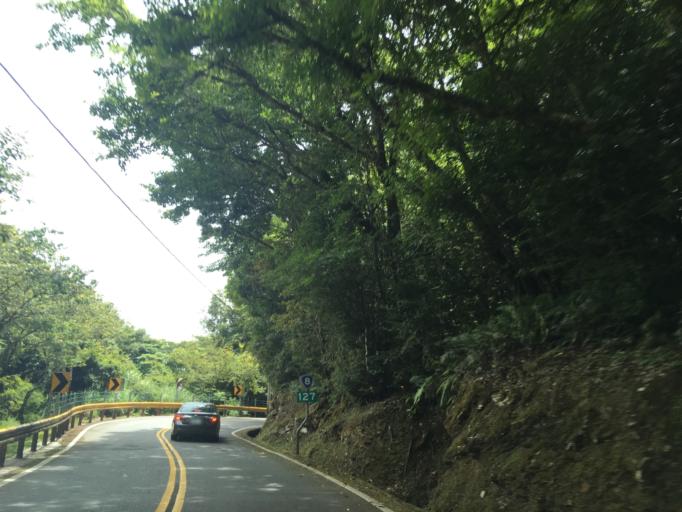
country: TW
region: Taiwan
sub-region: Hualien
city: Hualian
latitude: 24.1810
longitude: 121.3976
